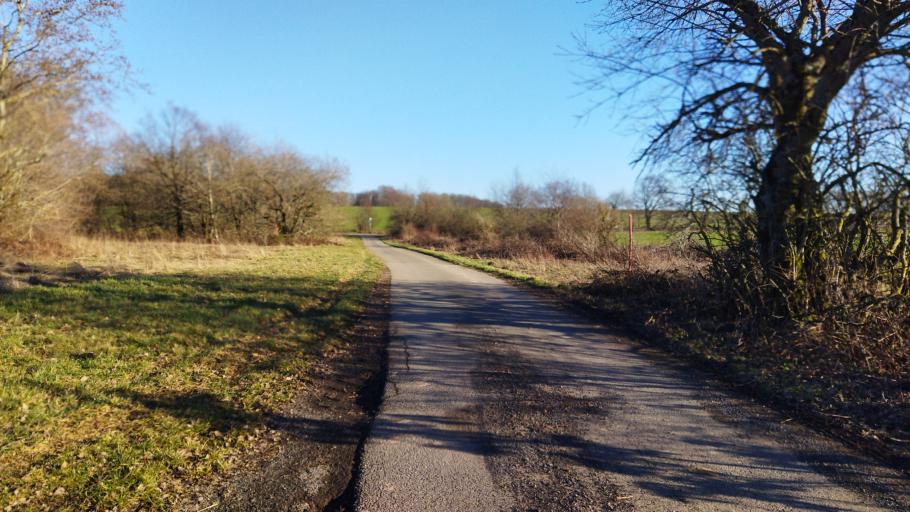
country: DE
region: Rheinland-Pfalz
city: Selchenbach
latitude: 49.4780
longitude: 7.3048
